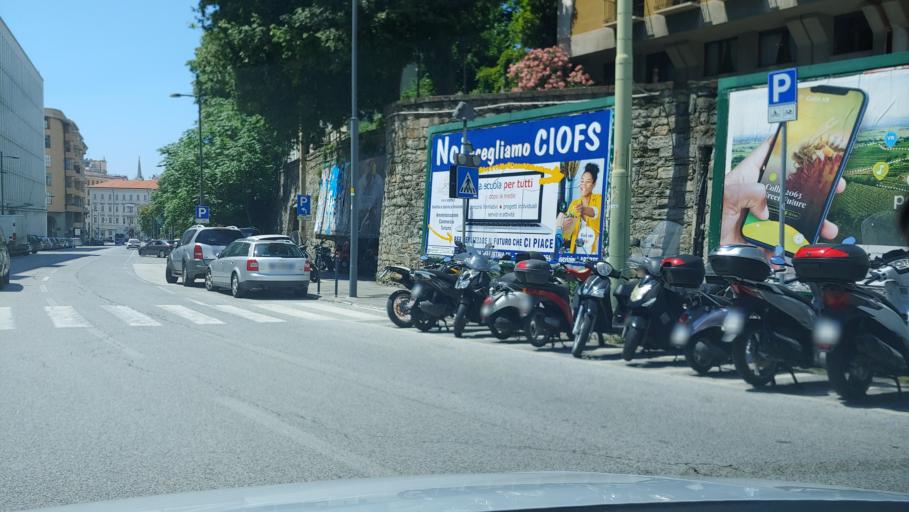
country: IT
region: Friuli Venezia Giulia
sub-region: Provincia di Trieste
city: Trieste
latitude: 45.6555
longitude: 13.7787
